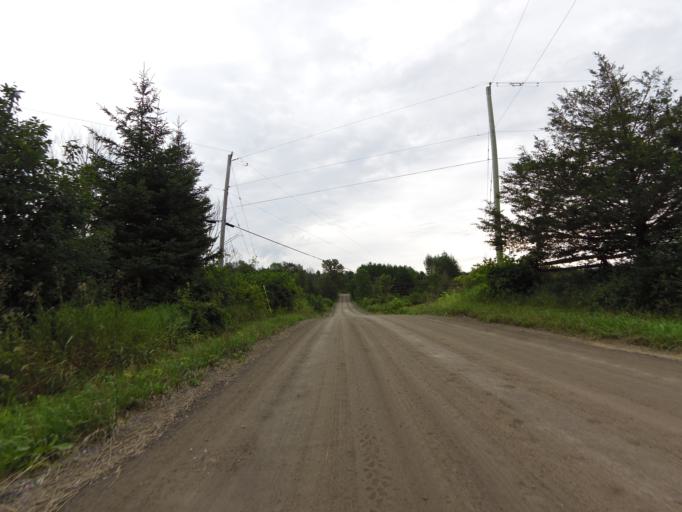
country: CA
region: Ontario
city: Kingston
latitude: 44.5546
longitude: -76.6219
